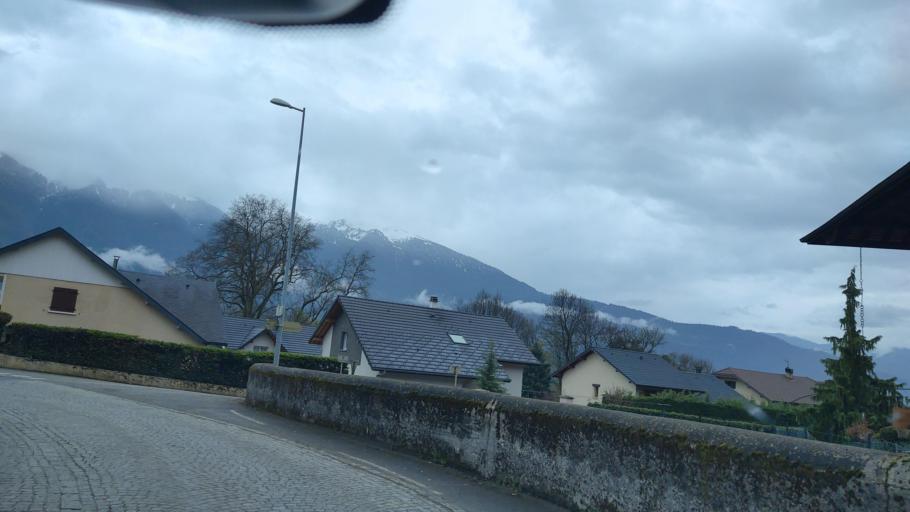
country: FR
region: Rhone-Alpes
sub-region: Departement de la Savoie
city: Frontenex
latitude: 45.6389
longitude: 6.3053
